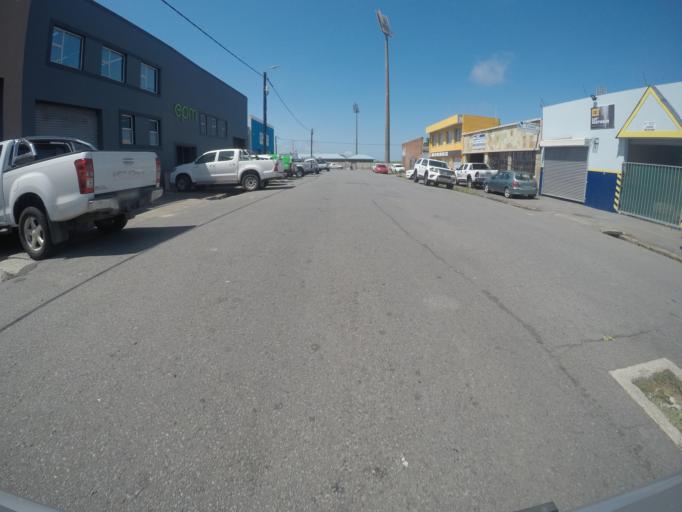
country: ZA
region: Eastern Cape
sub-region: Buffalo City Metropolitan Municipality
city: East London
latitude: -33.0081
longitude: 27.9047
